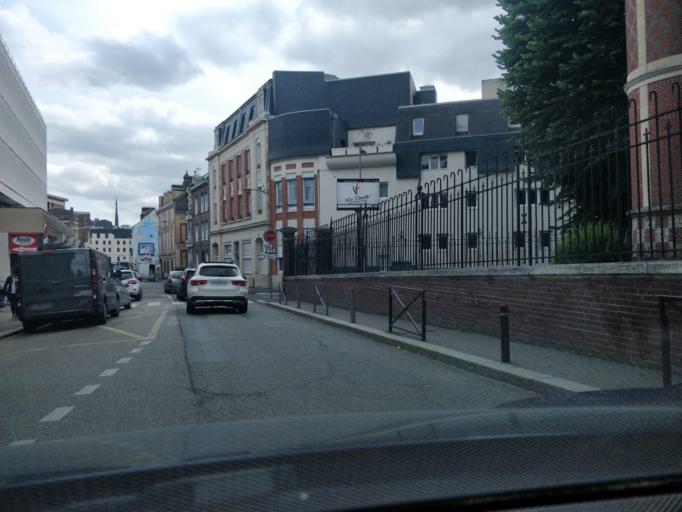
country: FR
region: Haute-Normandie
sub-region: Departement de la Seine-Maritime
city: Rouen
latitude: 49.4506
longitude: 1.0929
